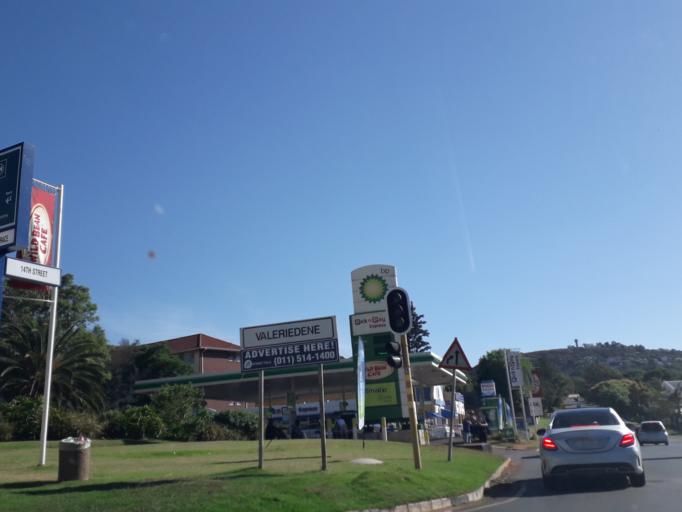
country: ZA
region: Gauteng
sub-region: City of Johannesburg Metropolitan Municipality
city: Roodepoort
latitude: -26.1449
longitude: 27.9535
